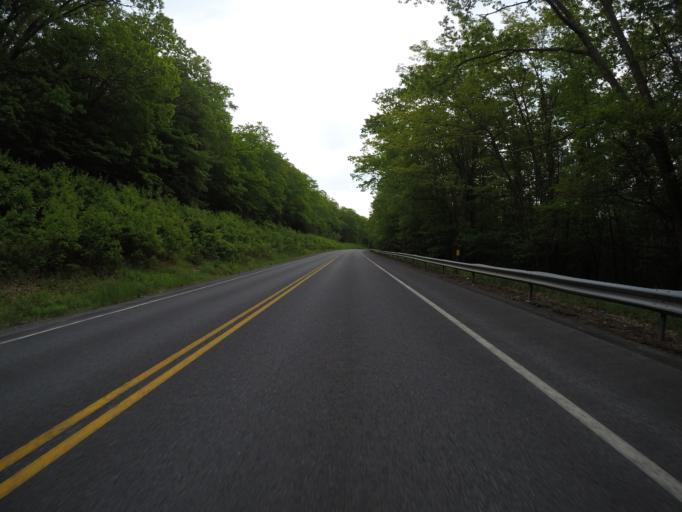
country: US
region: New York
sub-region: Sullivan County
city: Livingston Manor
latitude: 42.0604
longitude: -74.9238
